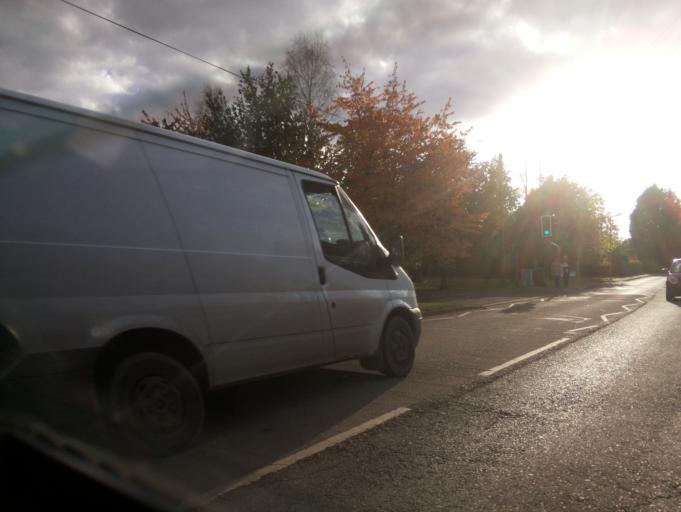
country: GB
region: England
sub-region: Herefordshire
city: Withington
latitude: 52.0668
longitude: -2.6448
